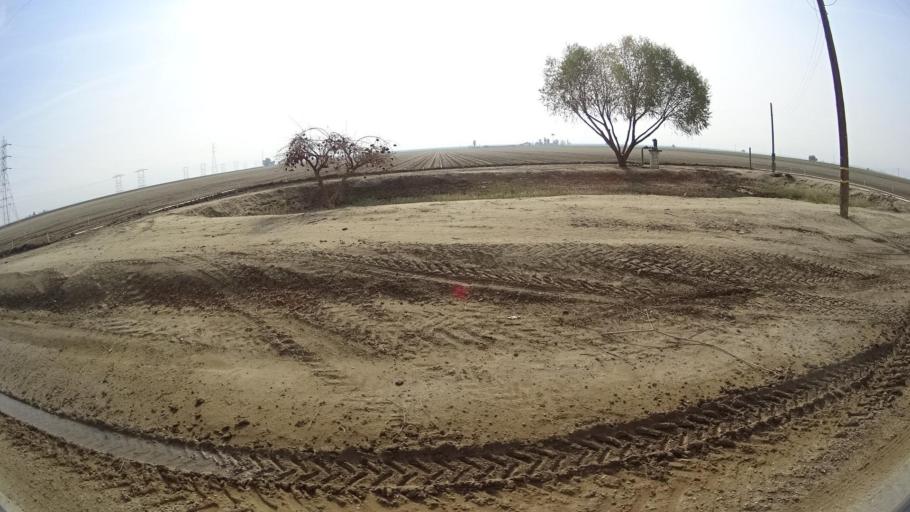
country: US
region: California
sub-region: Kern County
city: Arvin
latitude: 35.0454
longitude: -118.8769
